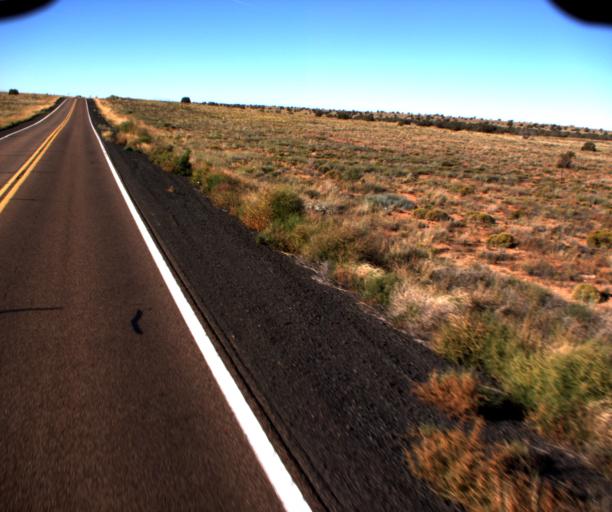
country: US
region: Arizona
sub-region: Navajo County
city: Holbrook
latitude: 34.7635
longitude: -110.2470
